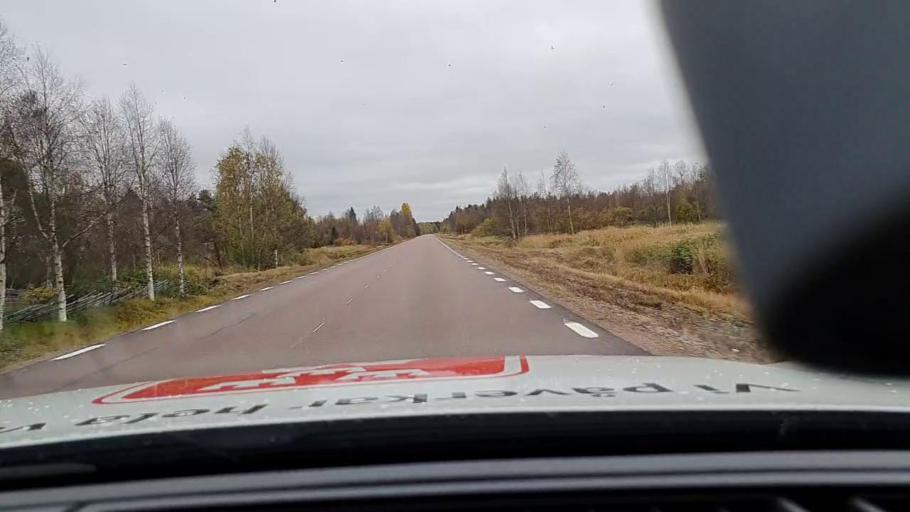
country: FI
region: Lapland
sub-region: Kemi-Tornio
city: Tornio
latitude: 66.0573
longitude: 23.9316
